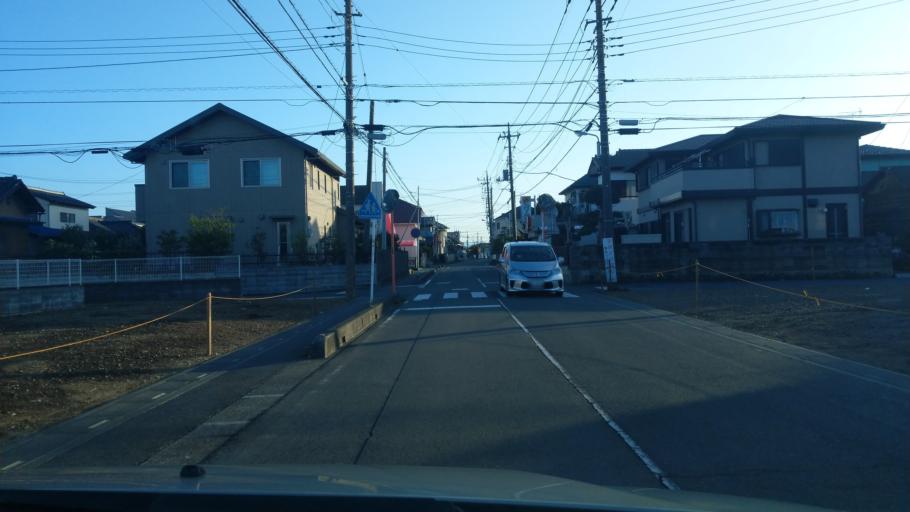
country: JP
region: Saitama
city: Yono
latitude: 35.9044
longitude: 139.5792
